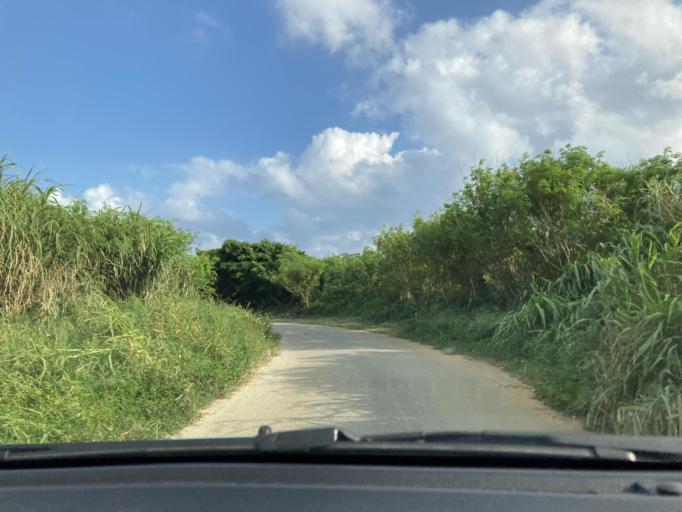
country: JP
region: Okinawa
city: Itoman
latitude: 26.0813
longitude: 127.6641
